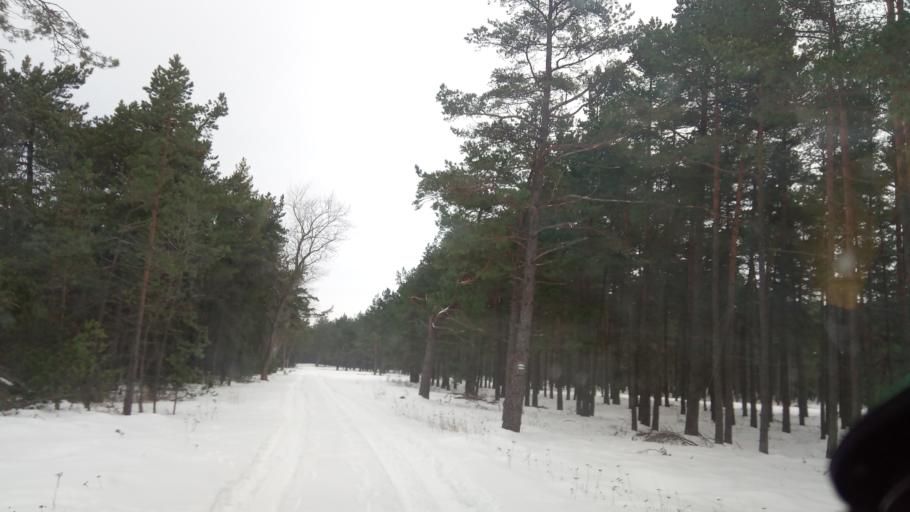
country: LT
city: Neringa
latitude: 55.4196
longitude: 21.0936
